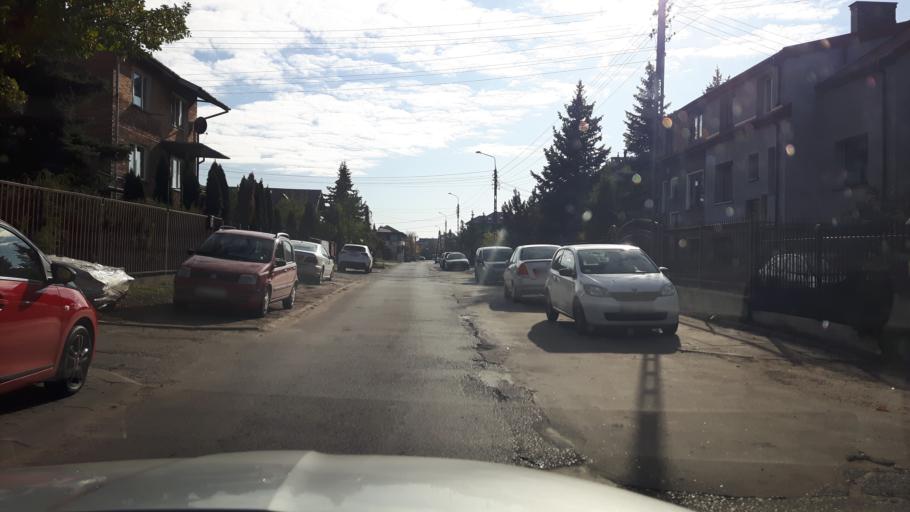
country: PL
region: Masovian Voivodeship
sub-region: Powiat wolominski
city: Zabki
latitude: 52.2993
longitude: 21.0987
